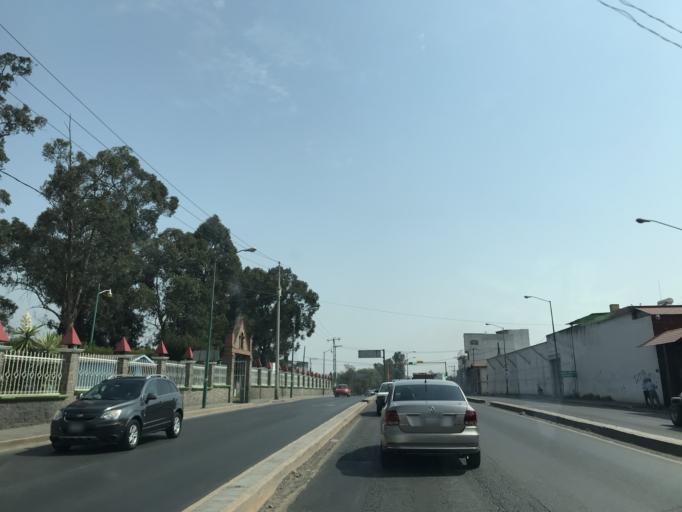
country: MX
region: Tlaxcala
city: Tlaxcala de Xicohtencatl
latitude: 19.3182
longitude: -98.2029
